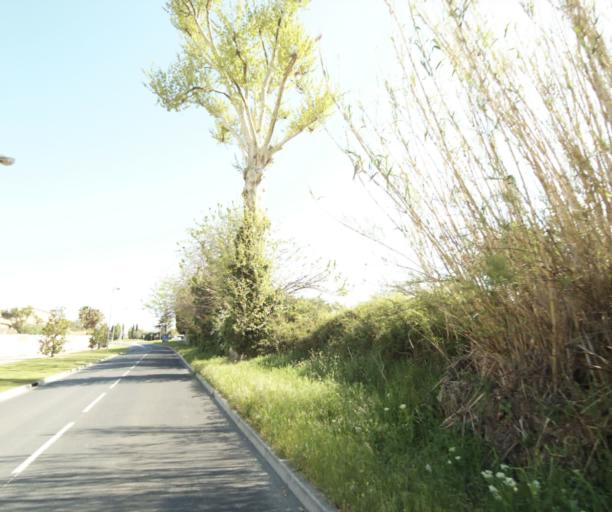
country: FR
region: Languedoc-Roussillon
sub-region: Departement de l'Herault
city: Lattes
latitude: 43.5767
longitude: 3.9072
